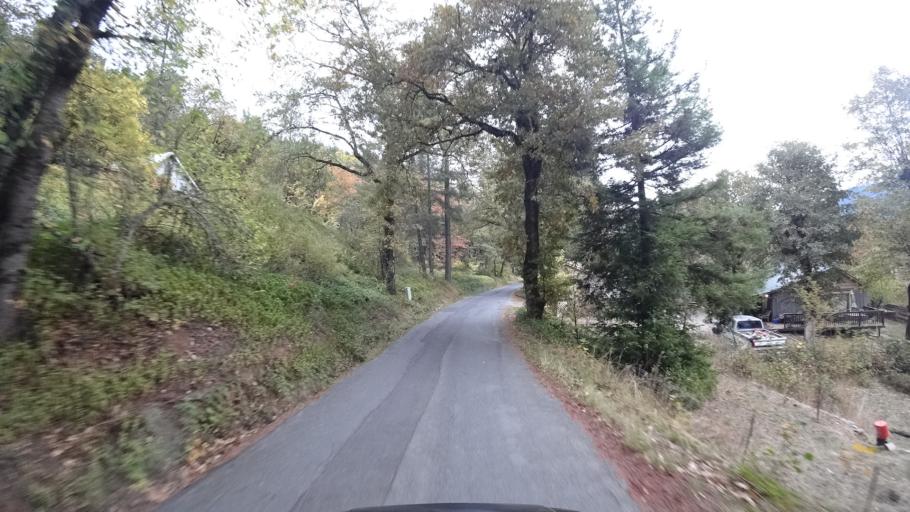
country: US
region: California
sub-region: Siskiyou County
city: Happy Camp
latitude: 41.7914
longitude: -123.3834
